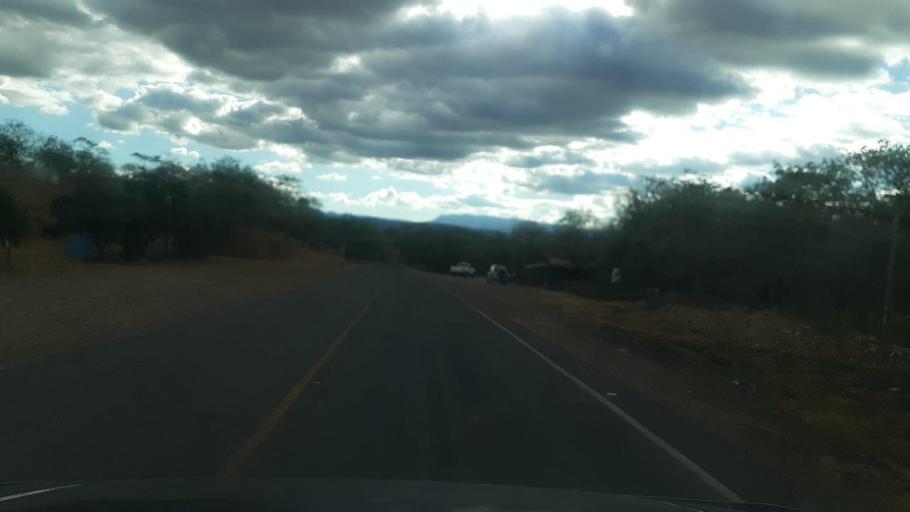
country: NI
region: Madriz
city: Somoto
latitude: 13.4732
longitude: -86.6013
